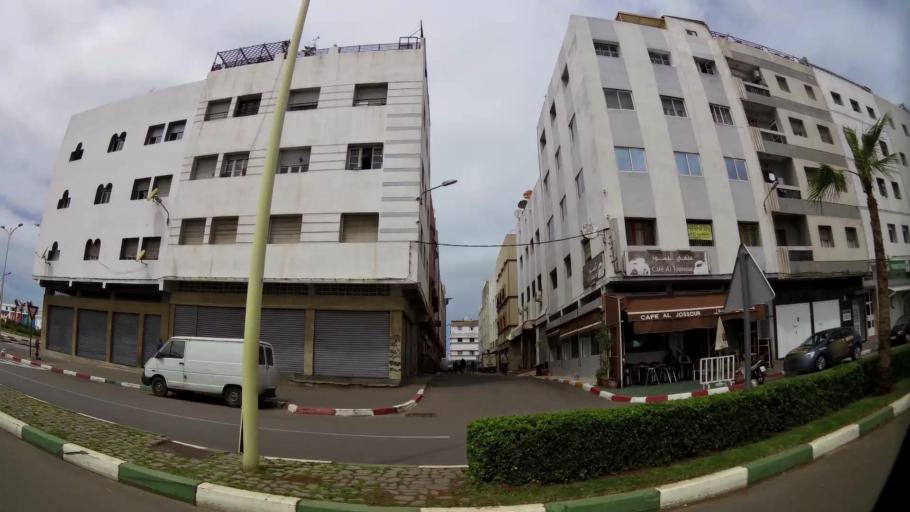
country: MA
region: Grand Casablanca
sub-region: Mediouna
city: Tit Mellil
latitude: 33.6035
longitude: -7.5081
